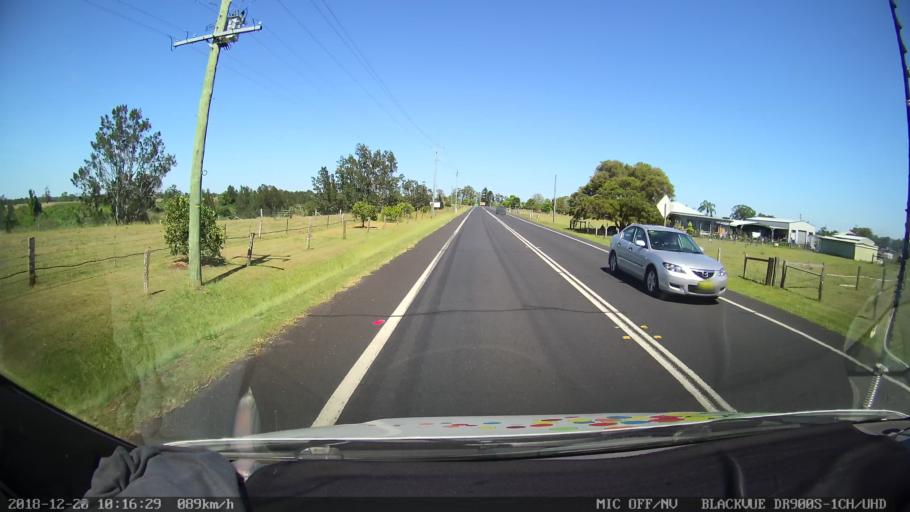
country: AU
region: New South Wales
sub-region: Richmond Valley
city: Casino
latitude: -28.8624
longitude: 153.0839
